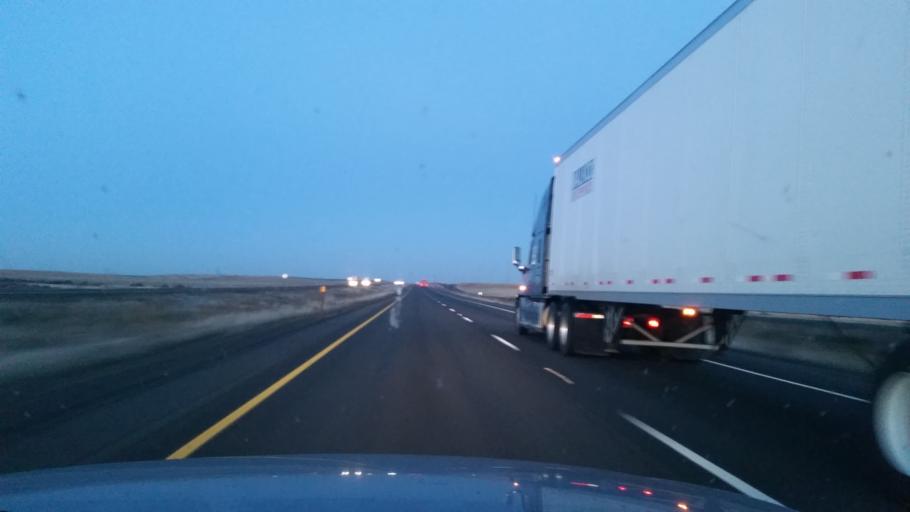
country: US
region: Washington
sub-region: Adams County
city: Ritzville
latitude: 47.1692
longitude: -118.2900
